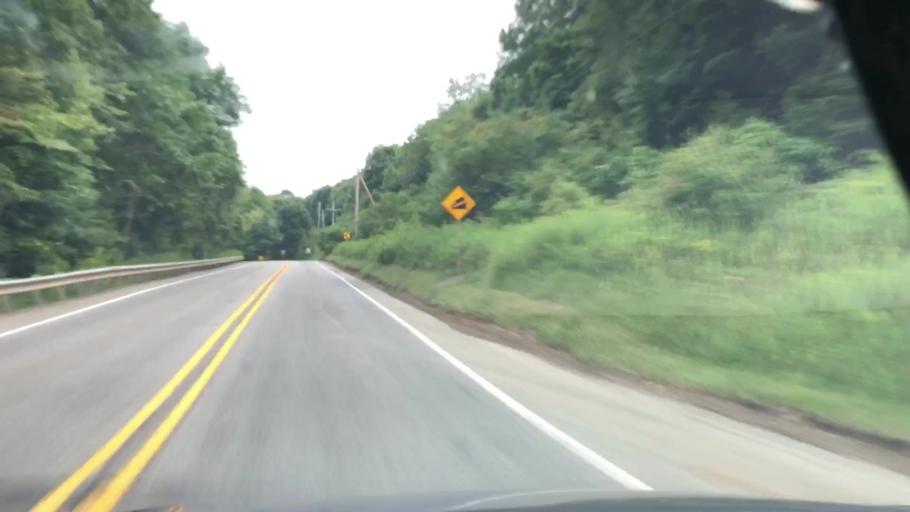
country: US
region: Pennsylvania
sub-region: Venango County
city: Hasson Heights
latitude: 41.5227
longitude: -79.7100
